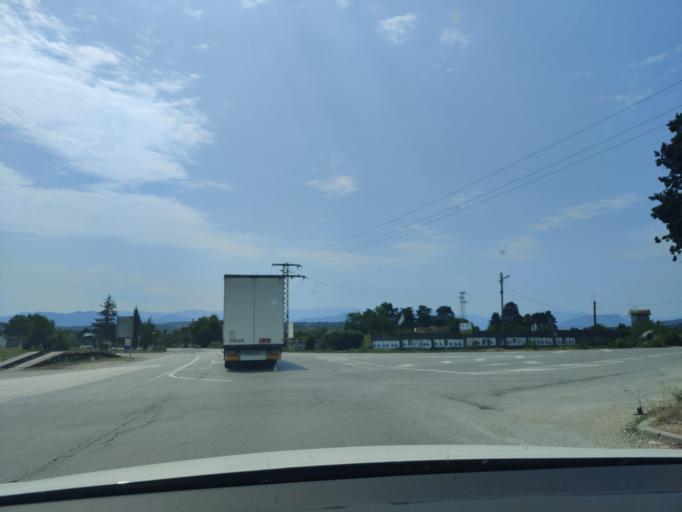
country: BG
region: Vidin
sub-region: Obshtina Ruzhintsi
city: Ruzhintsi
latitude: 43.6208
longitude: 22.8181
